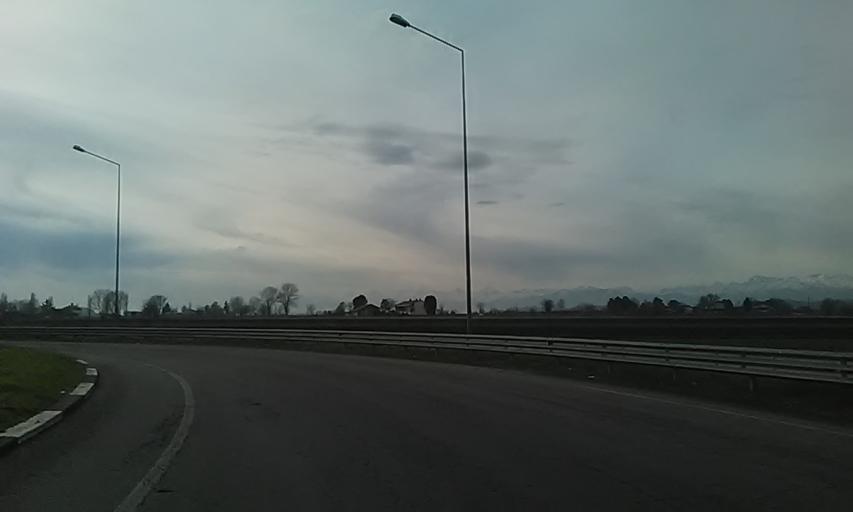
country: IT
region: Piedmont
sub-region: Provincia di Vercelli
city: Cigliano
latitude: 45.2983
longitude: 8.0062
